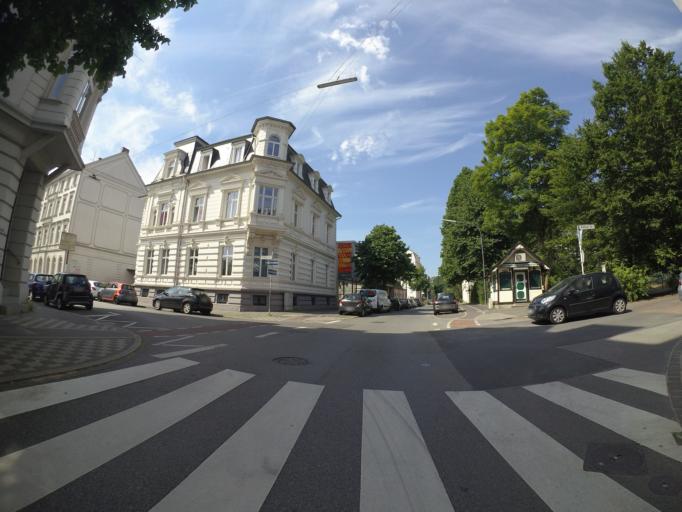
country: DE
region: North Rhine-Westphalia
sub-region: Regierungsbezirk Dusseldorf
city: Wuppertal
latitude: 51.2633
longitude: 7.1733
